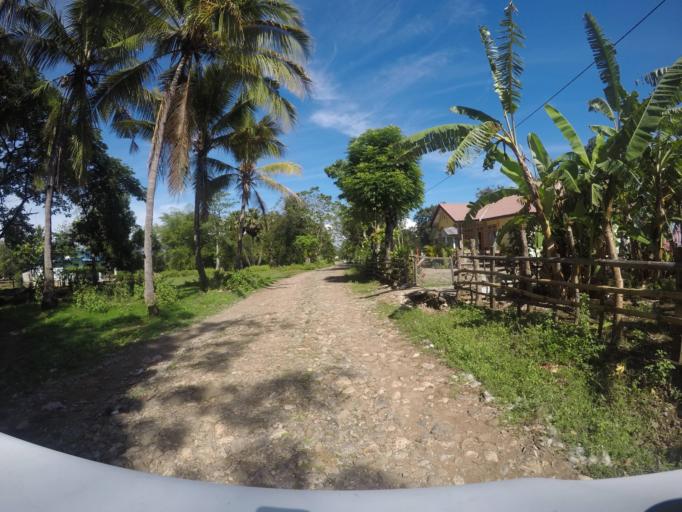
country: TL
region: Bobonaro
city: Maliana
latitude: -8.9874
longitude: 125.1963
